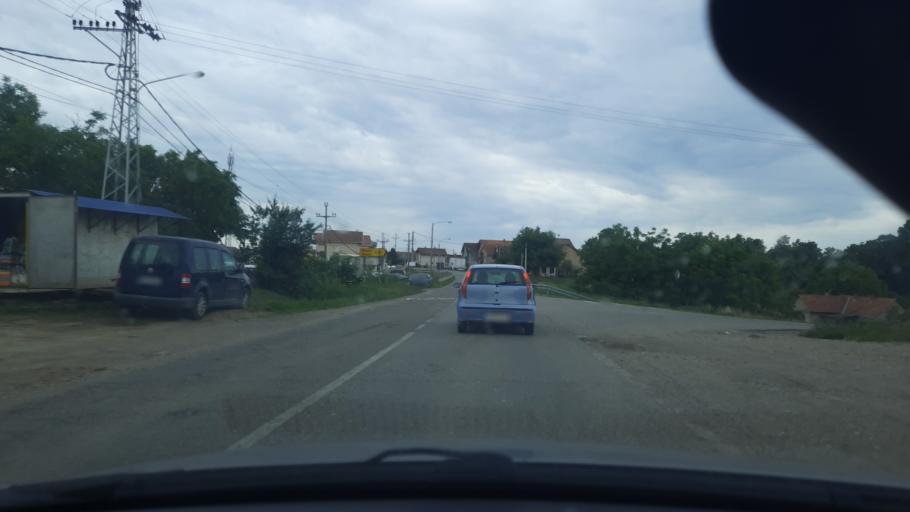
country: RS
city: Jevremovac
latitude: 44.7208
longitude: 19.6632
